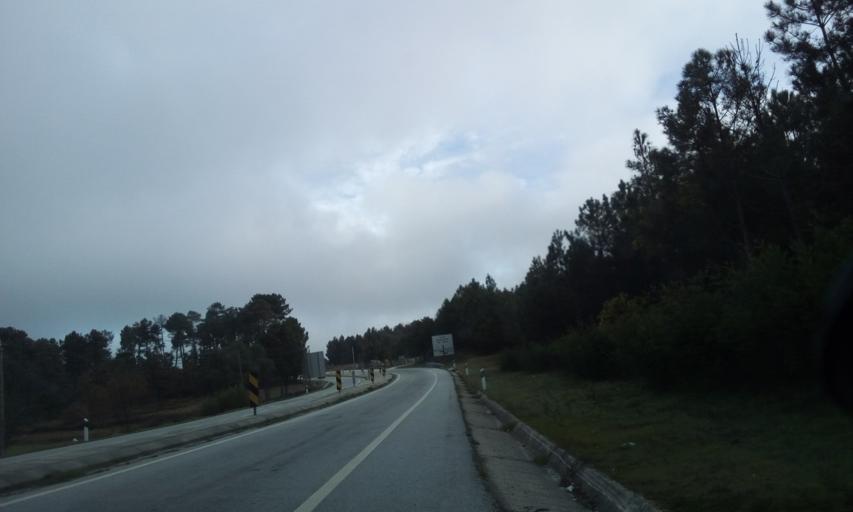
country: PT
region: Guarda
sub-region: Aguiar da Beira
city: Aguiar da Beira
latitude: 40.7319
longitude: -7.4945
